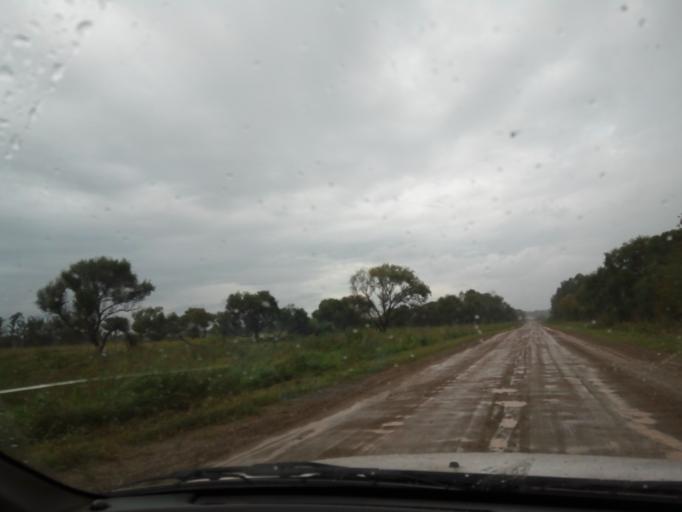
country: RU
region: Primorskiy
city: Lazo
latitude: 45.8466
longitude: 133.6450
